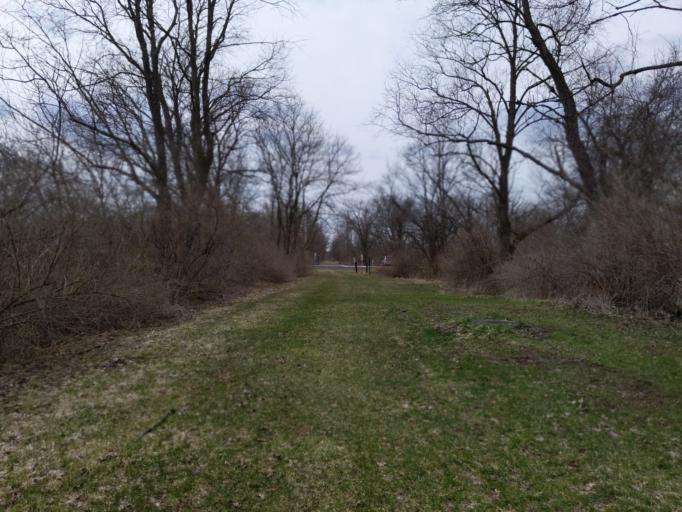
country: US
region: New York
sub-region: Tompkins County
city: Dryden
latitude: 42.4963
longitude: -76.3130
